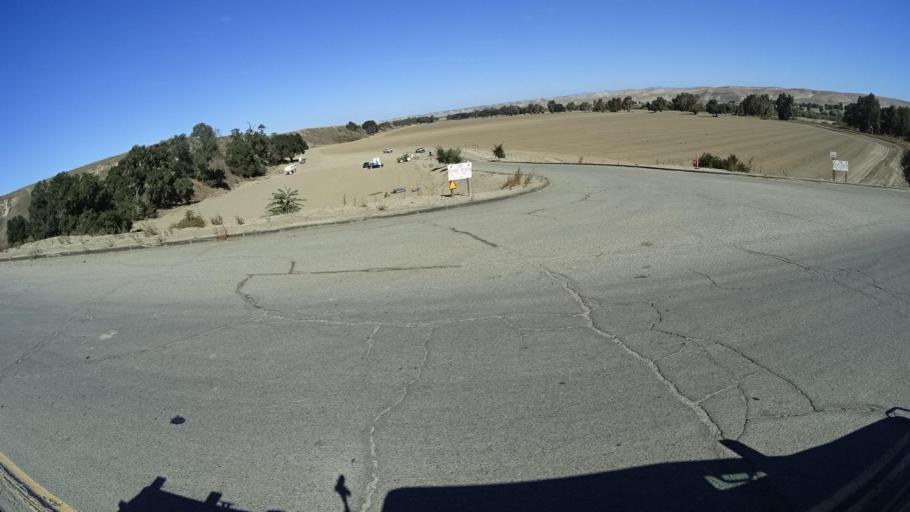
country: US
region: California
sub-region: Monterey County
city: King City
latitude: 36.0134
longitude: -120.9192
